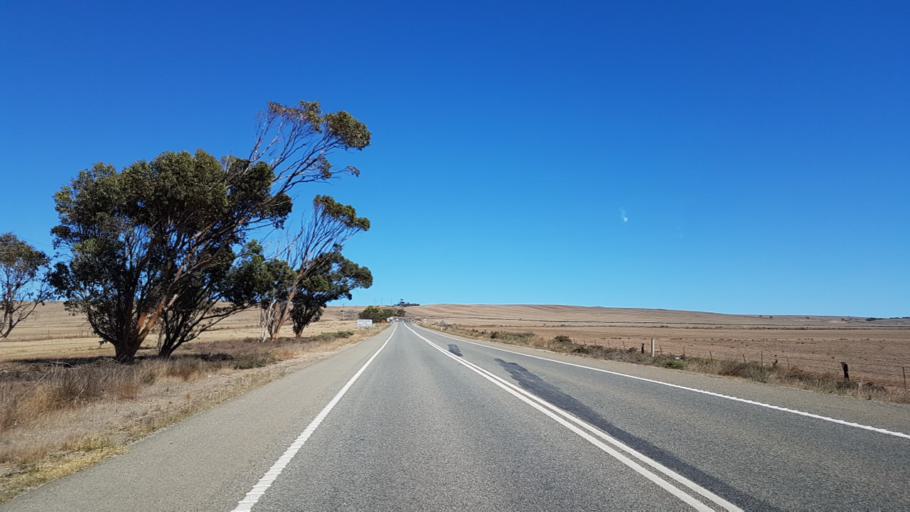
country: AU
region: South Australia
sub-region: Wakefield
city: Balaklava
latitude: -34.0705
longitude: 138.0691
